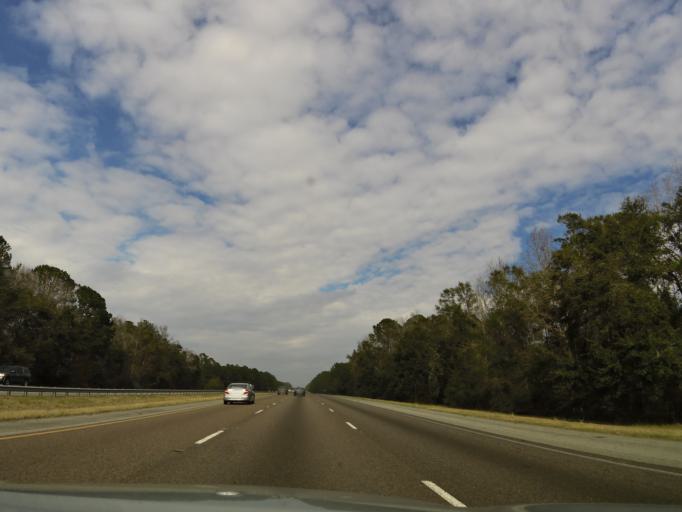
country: US
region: Georgia
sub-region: Liberty County
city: Midway
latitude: 31.8388
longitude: -81.3499
